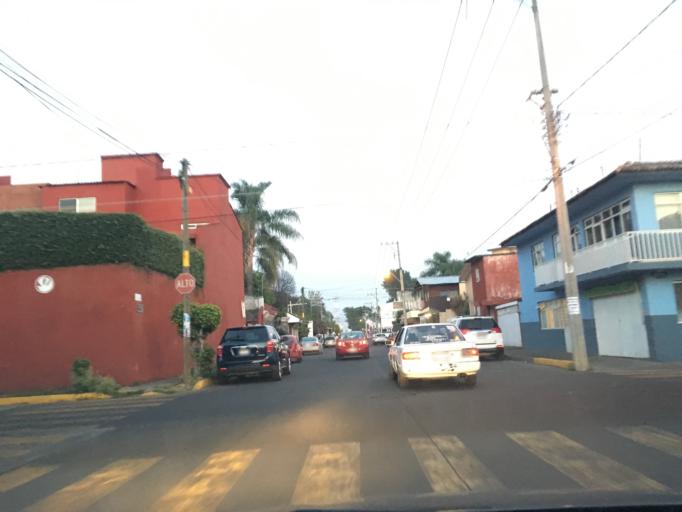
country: MX
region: Michoacan
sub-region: Uruapan
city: Uruapan
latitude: 19.4098
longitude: -102.0553
